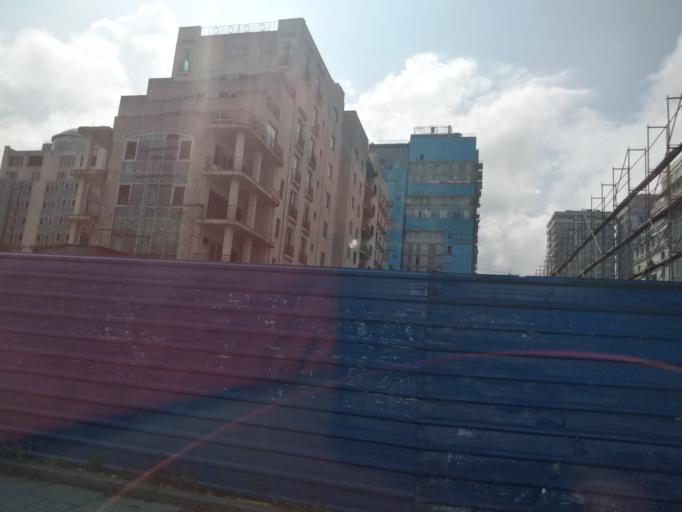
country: GE
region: Ajaria
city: Batumi
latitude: 41.6447
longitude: 41.6172
